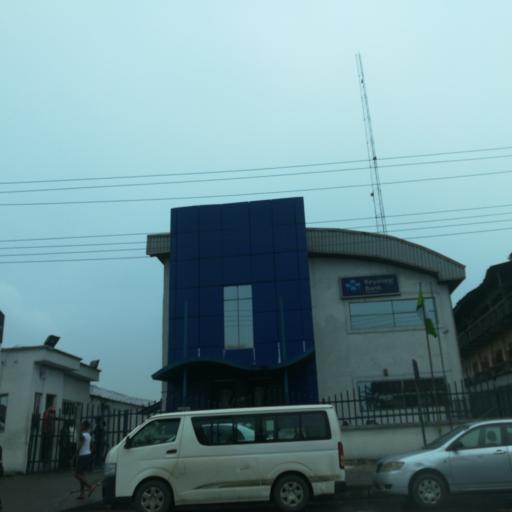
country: NG
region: Rivers
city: Port Harcourt
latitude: 4.7961
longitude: 6.9936
